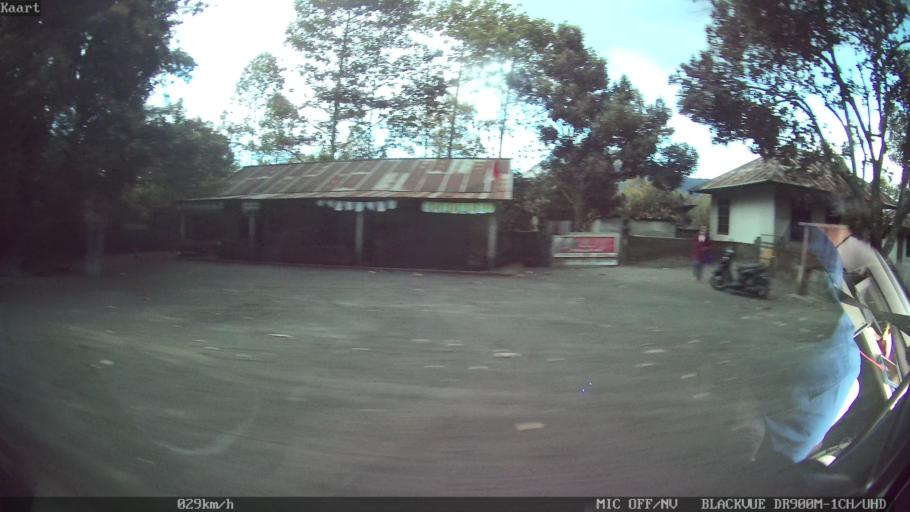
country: ID
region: Bali
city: Banjar Kedisan
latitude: -8.2492
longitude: 115.3472
